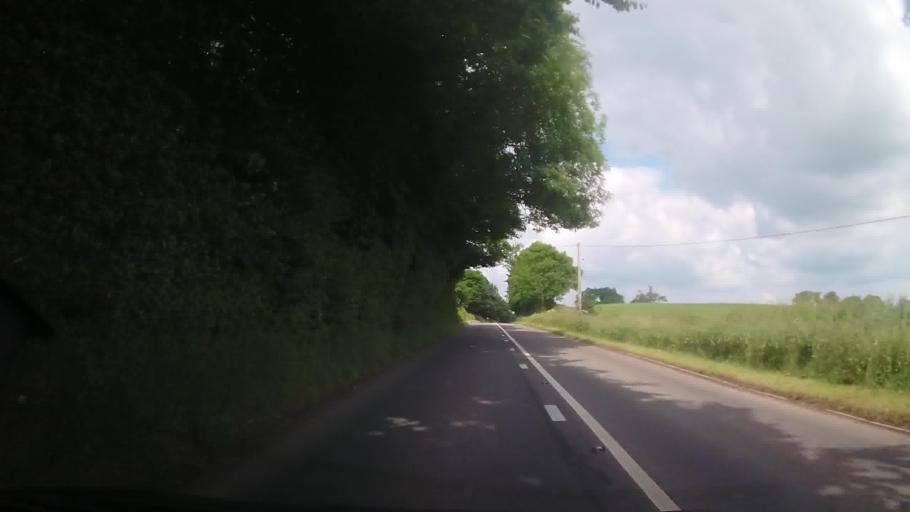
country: GB
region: England
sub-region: Shropshire
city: Ellesmere
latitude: 52.8985
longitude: -2.9263
